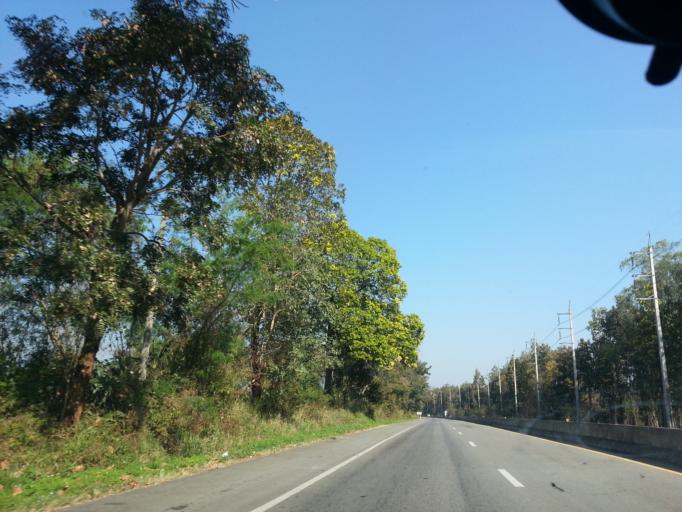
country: TH
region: Chiang Mai
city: Mae Taeng
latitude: 19.1546
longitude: 98.9482
